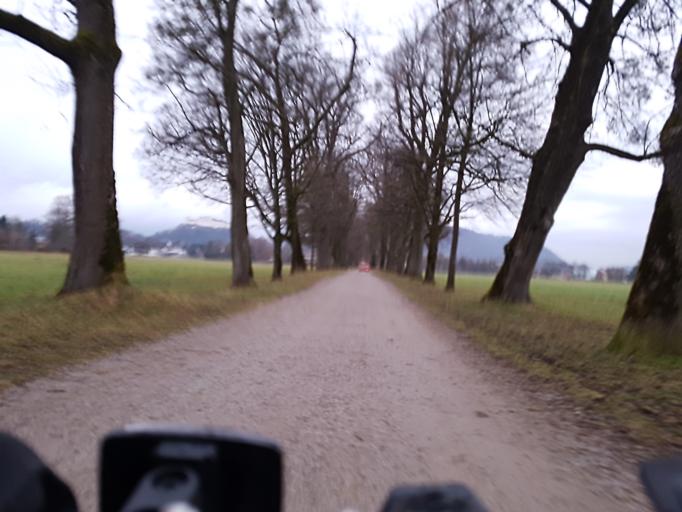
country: AT
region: Salzburg
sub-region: Salzburg Stadt
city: Salzburg
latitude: 47.7806
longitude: 13.0593
